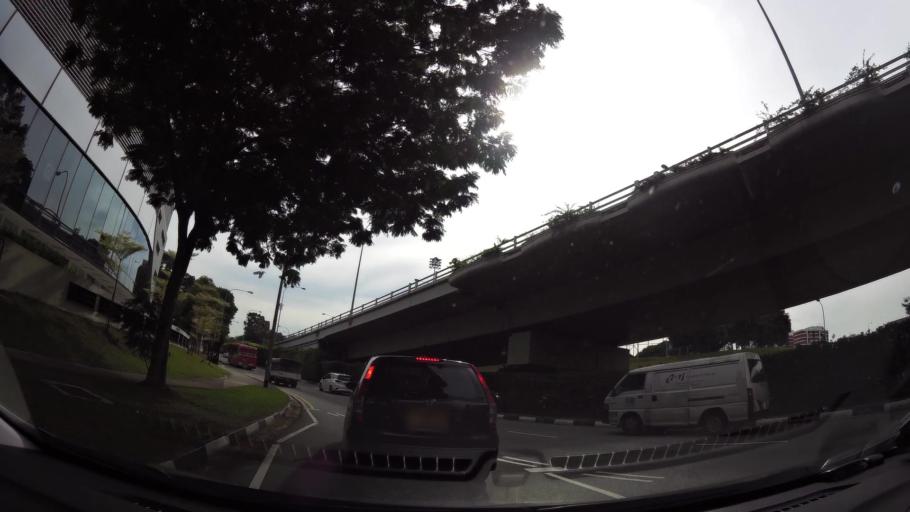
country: SG
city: Singapore
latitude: 1.3371
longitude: 103.7789
